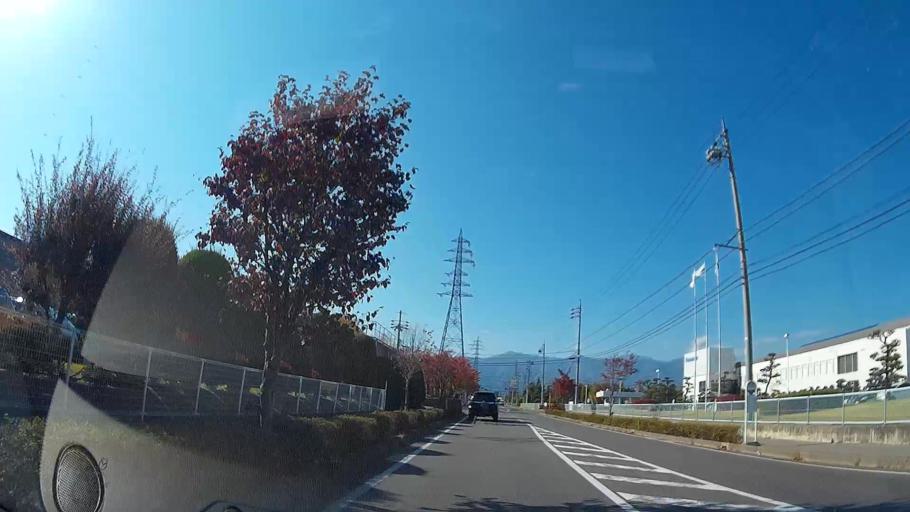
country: JP
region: Nagano
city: Matsumoto
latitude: 36.2048
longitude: 137.9369
